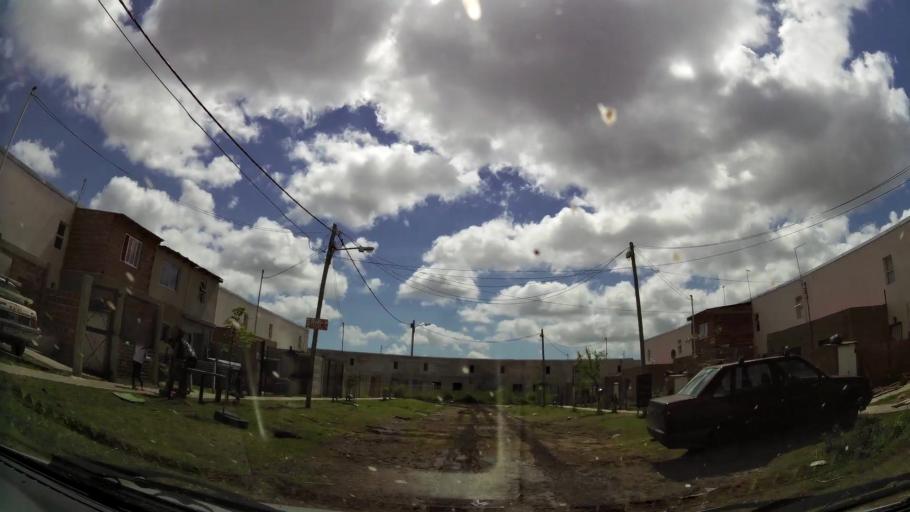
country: AR
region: Buenos Aires
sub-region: Partido de Quilmes
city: Quilmes
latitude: -34.8296
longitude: -58.2105
